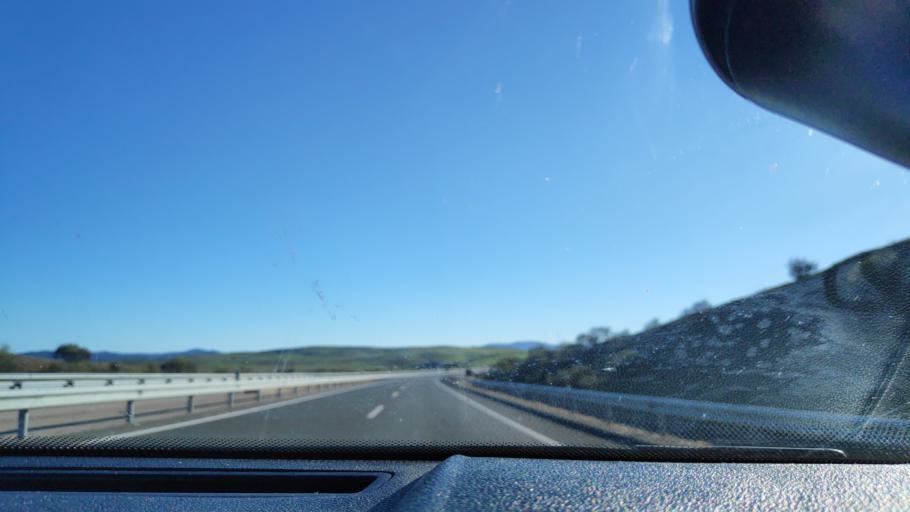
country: ES
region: Extremadura
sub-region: Provincia de Badajoz
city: Fuente de Cantos
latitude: 38.1754
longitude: -6.2792
